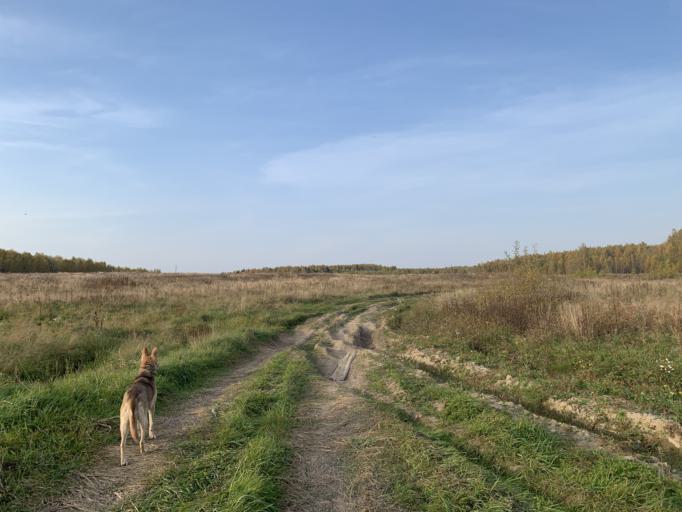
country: RU
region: Jaroslavl
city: Porech'ye-Rybnoye
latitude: 56.9832
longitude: 39.3838
